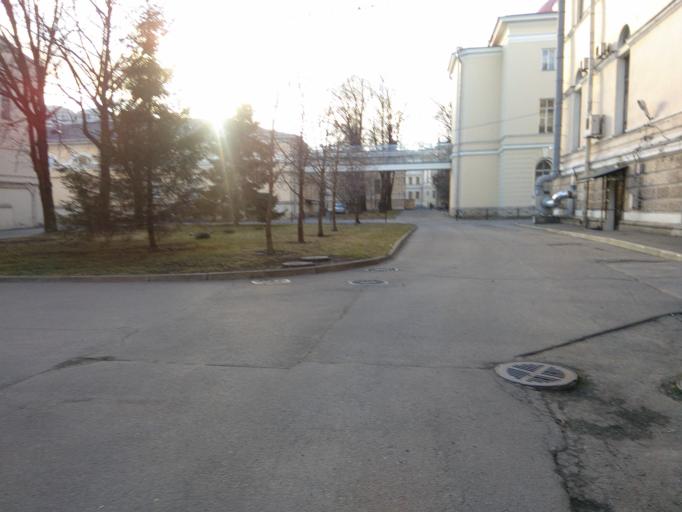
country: RU
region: St.-Petersburg
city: Saint Petersburg
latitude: 59.9443
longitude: 30.3028
